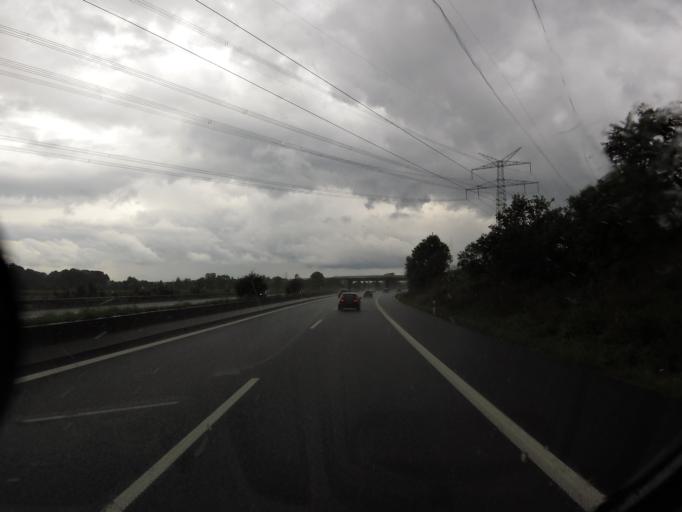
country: DE
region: Bavaria
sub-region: Upper Bavaria
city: Karlsfeld
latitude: 48.1964
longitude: 11.4369
